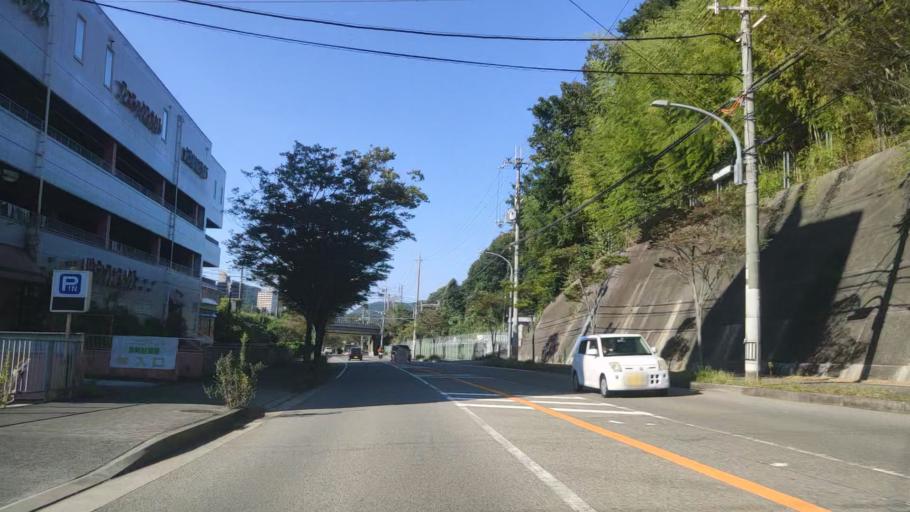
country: JP
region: Hyogo
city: Kobe
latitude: 34.7730
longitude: 135.1926
